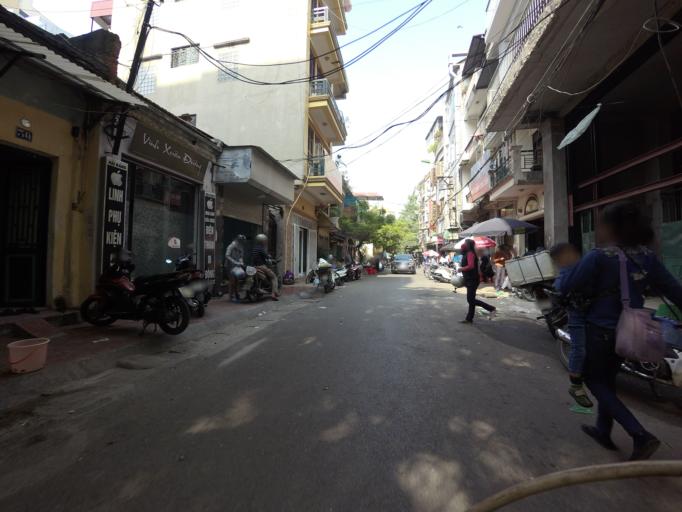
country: VN
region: Ha Noi
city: Hoan Kiem
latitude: 21.0455
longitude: 105.8409
